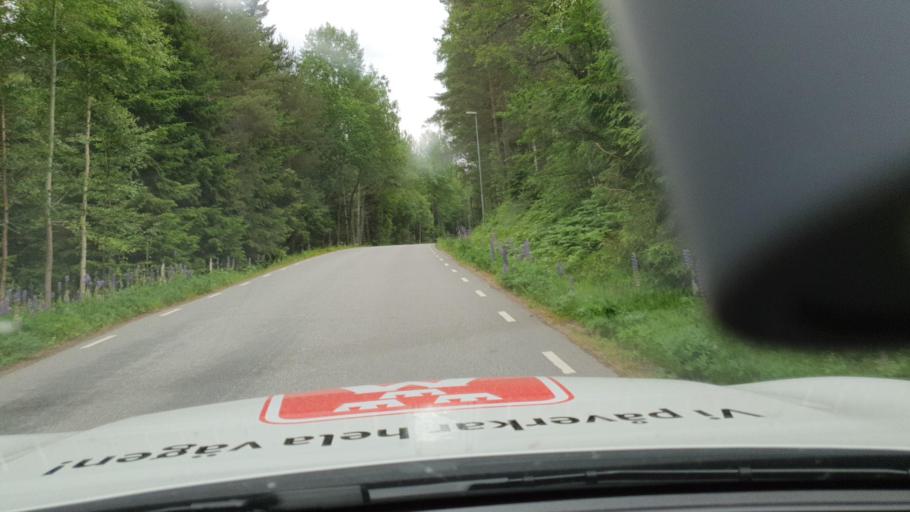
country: SE
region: Vaestra Goetaland
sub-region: Karlsborgs Kommun
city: Karlsborg
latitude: 58.6627
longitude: 14.4112
